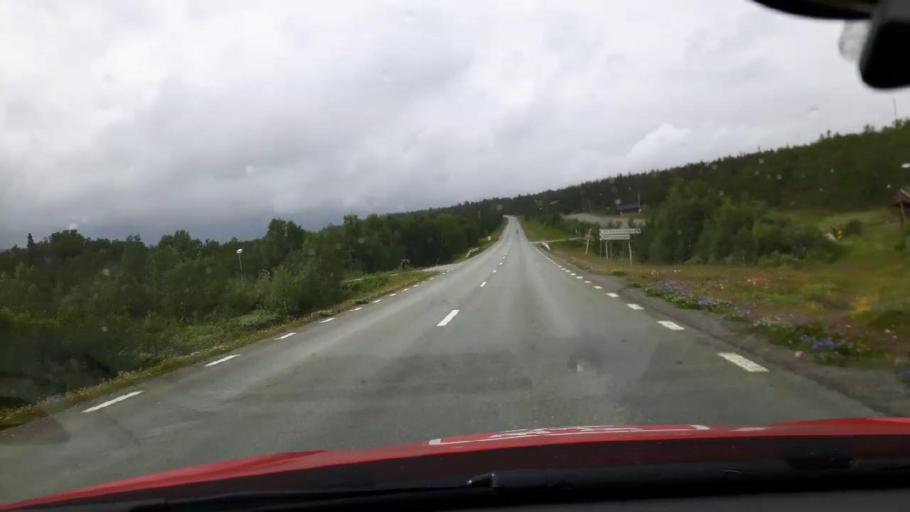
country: NO
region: Nord-Trondelag
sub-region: Meraker
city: Meraker
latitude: 63.2880
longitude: 12.1236
